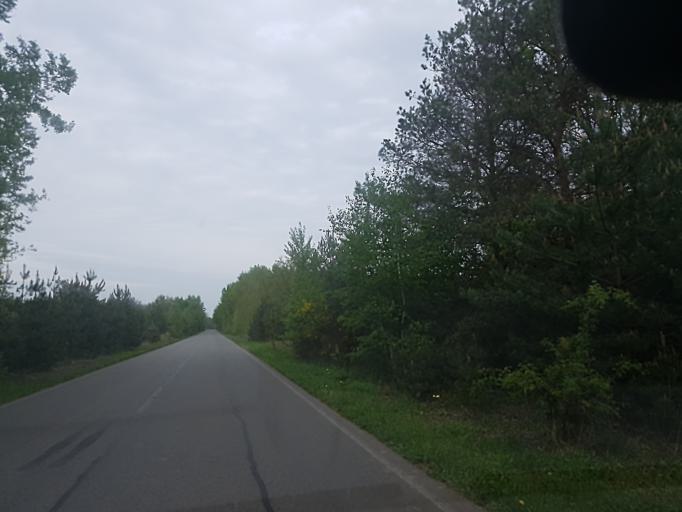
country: DE
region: Brandenburg
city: Finsterwalde
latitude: 51.6070
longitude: 13.7612
